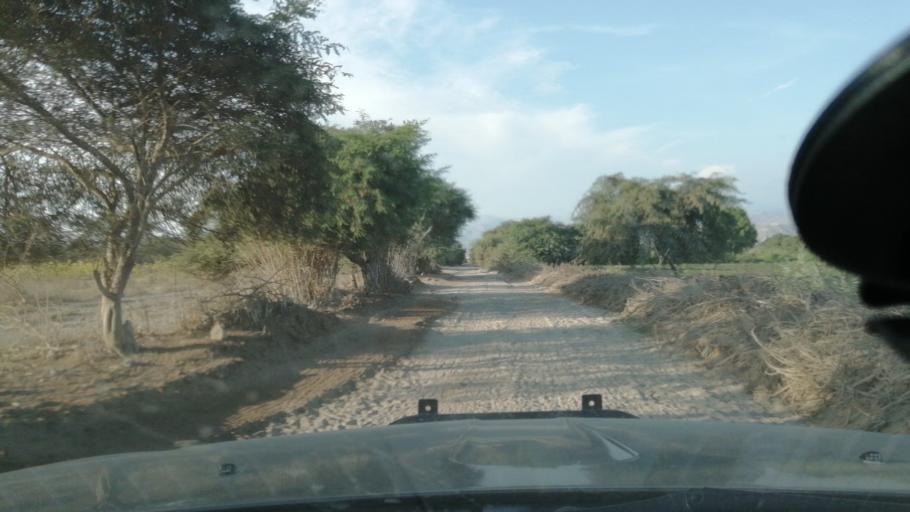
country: PE
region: Ica
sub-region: Provincia de Chincha
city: San Pedro
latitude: -13.3451
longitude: -76.1604
